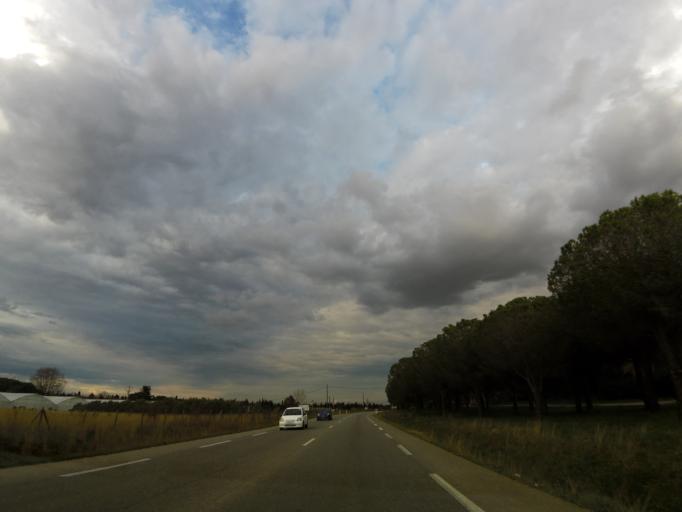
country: FR
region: Languedoc-Roussillon
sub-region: Departement du Gard
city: Vestric-et-Candiac
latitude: 43.7304
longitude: 4.2724
